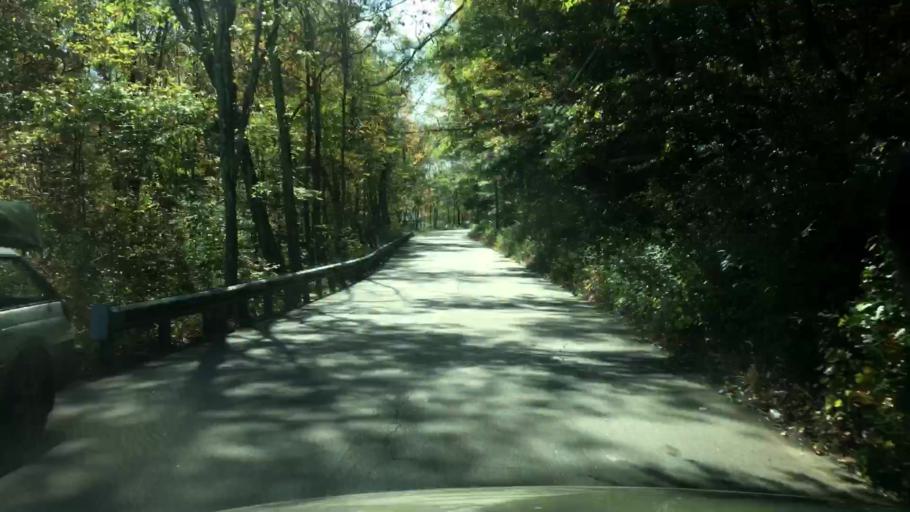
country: US
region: Connecticut
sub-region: Tolland County
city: Stafford Springs
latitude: 41.9679
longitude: -72.2983
